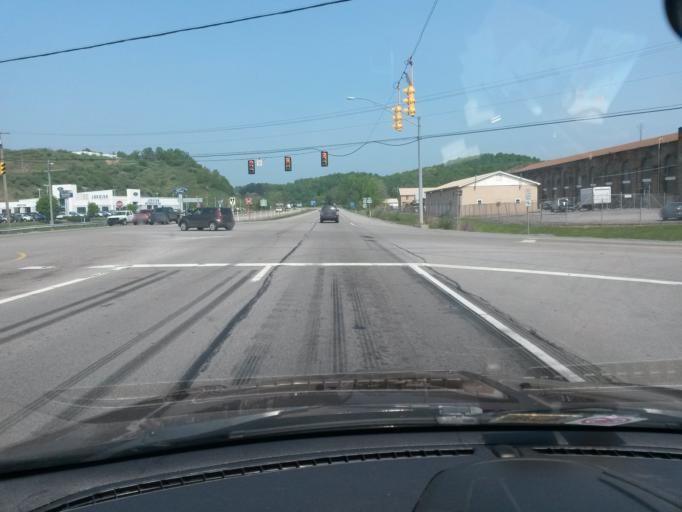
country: US
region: West Virginia
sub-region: Upshur County
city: Buckhannon
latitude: 38.9992
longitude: -80.2516
